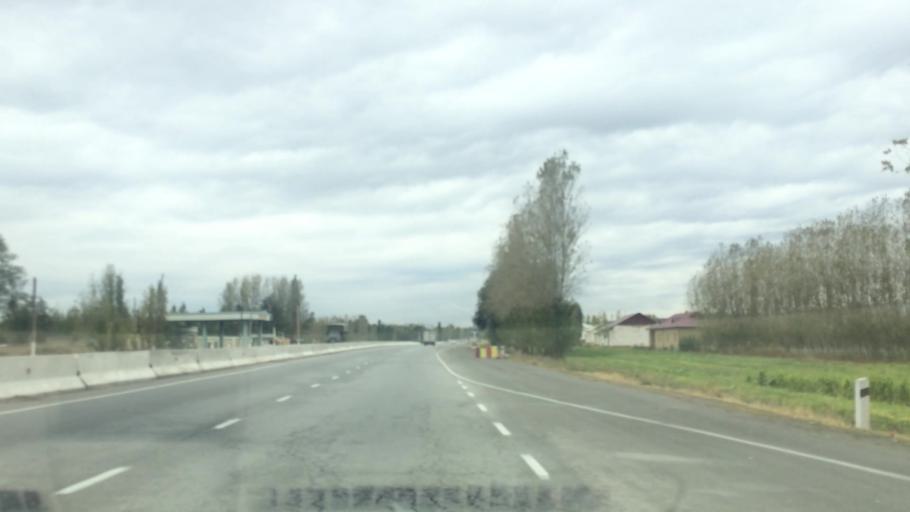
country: UZ
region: Jizzax
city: Jizzax
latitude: 39.9627
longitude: 67.5486
